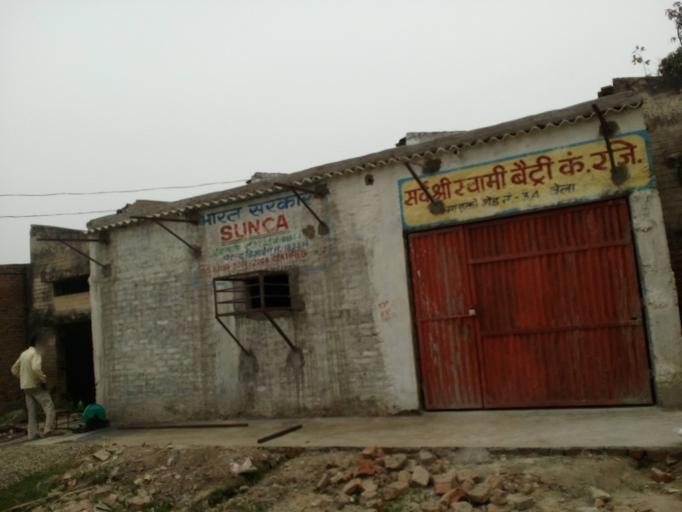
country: IN
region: Bihar
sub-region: Muzaffarpur
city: Muzaffarpur
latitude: 26.1018
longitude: 85.4099
